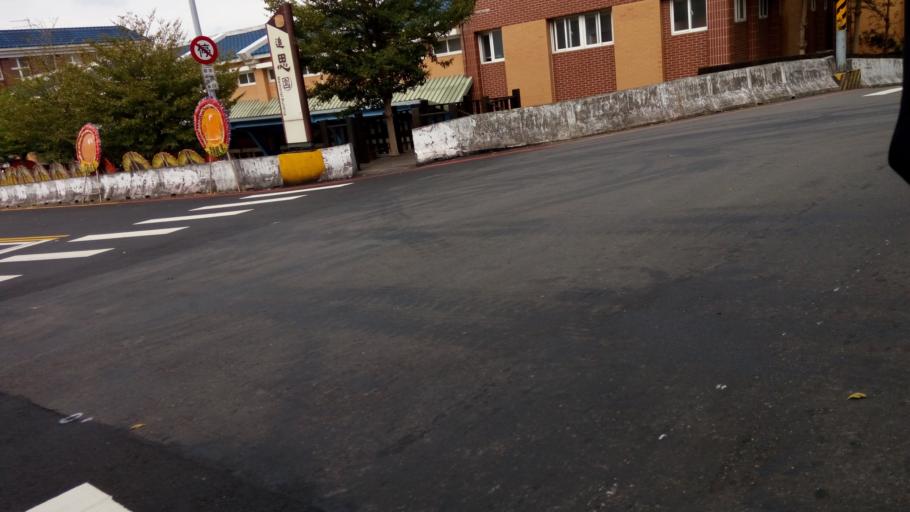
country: TW
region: Taiwan
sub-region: Hsinchu
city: Hsinchu
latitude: 24.7923
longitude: 120.9575
